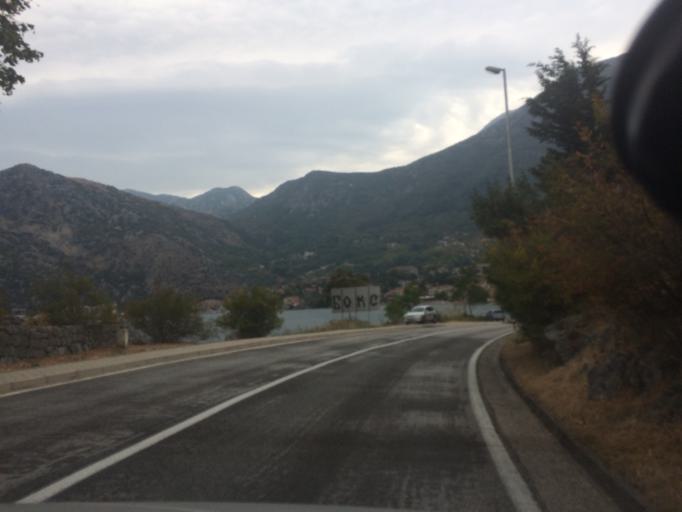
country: ME
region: Kotor
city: Risan
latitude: 42.5060
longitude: 18.6937
